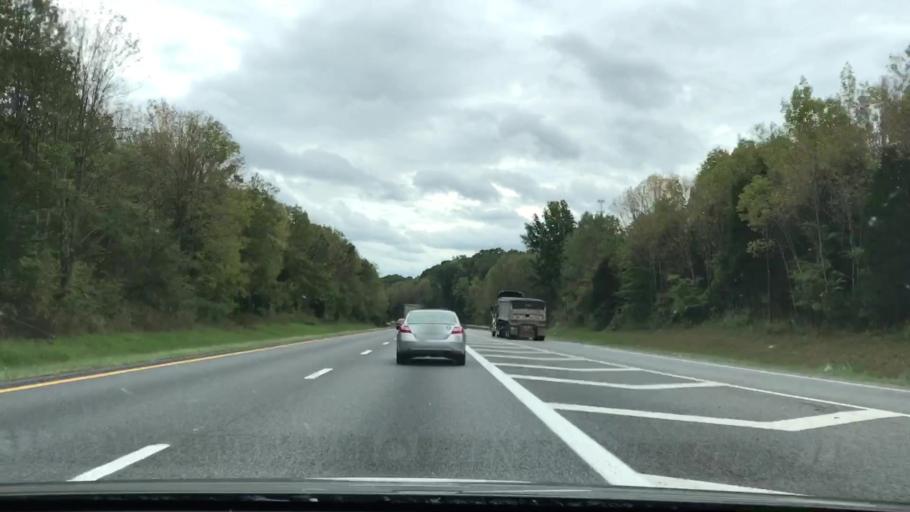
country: US
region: Tennessee
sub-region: Montgomery County
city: Clarksville
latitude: 36.5526
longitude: -87.2485
